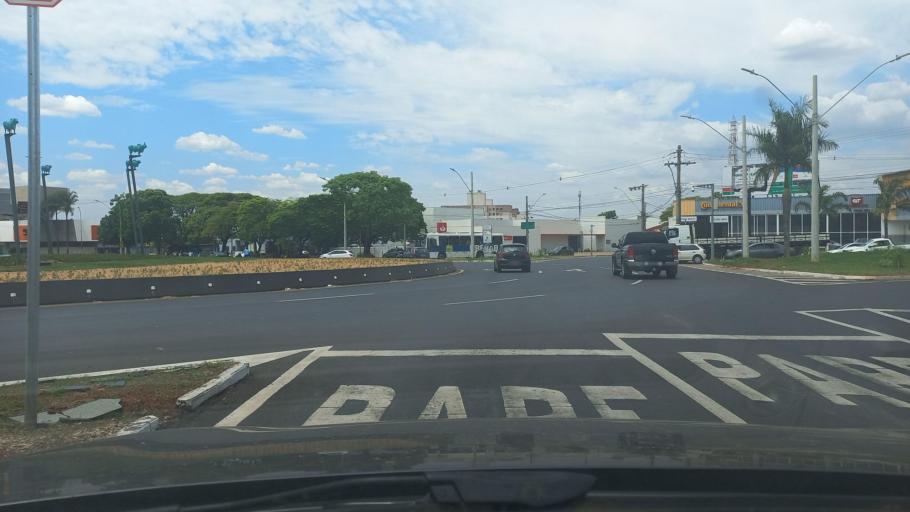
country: BR
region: Minas Gerais
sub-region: Uberaba
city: Uberaba
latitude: -19.7703
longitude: -47.9454
